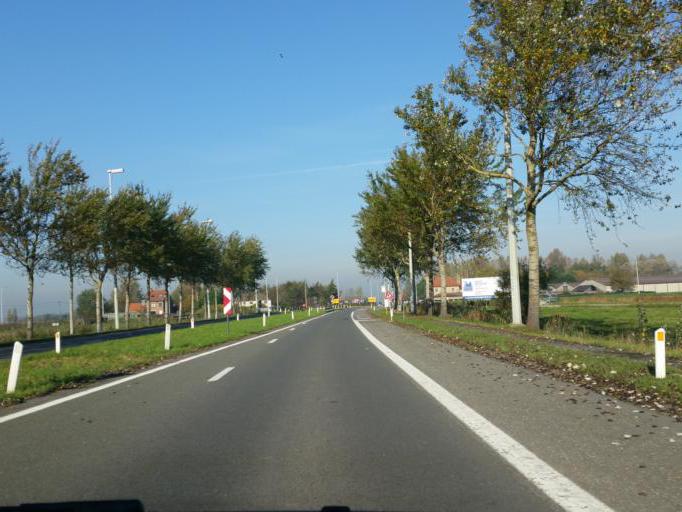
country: BE
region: Flanders
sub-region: Provincie West-Vlaanderen
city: De Haan
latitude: 51.2305
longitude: 3.0614
